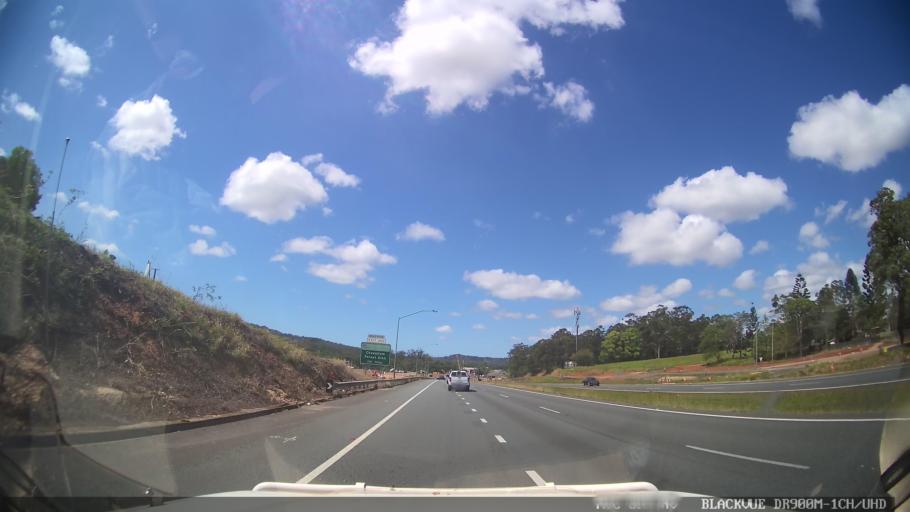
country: AU
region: Queensland
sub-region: Sunshine Coast
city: Woombye
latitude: -26.6761
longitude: 153.0005
